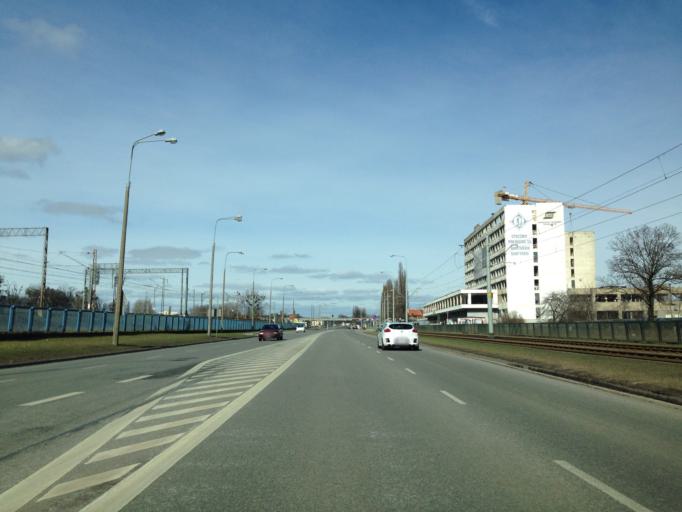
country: PL
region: Pomeranian Voivodeship
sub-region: Gdansk
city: Gdansk
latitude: 54.3702
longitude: 18.6358
